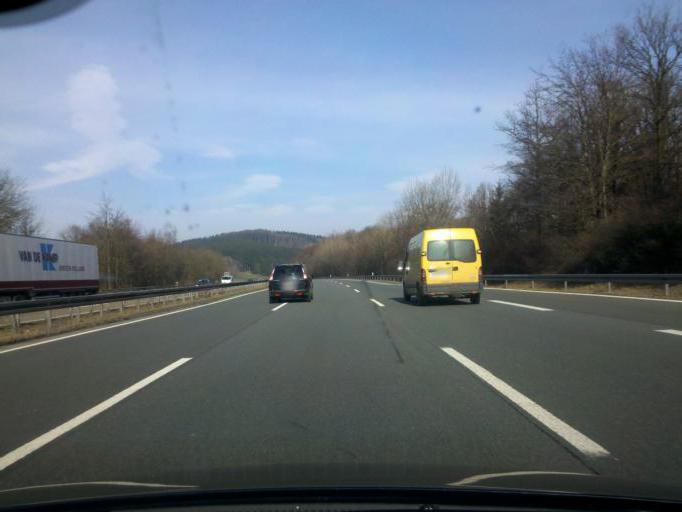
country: DE
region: North Rhine-Westphalia
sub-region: Regierungsbezirk Arnsberg
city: Drolshagen
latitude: 51.0460
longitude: 7.7965
